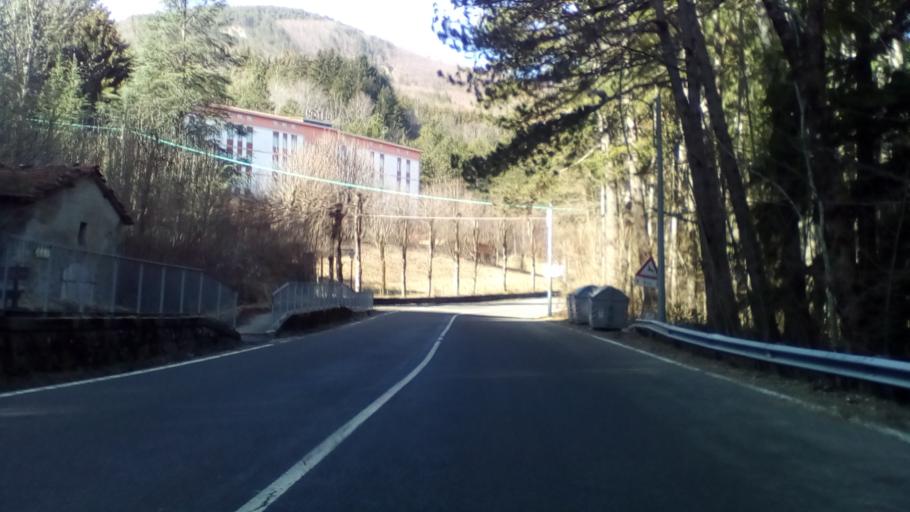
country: IT
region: Emilia-Romagna
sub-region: Provincia di Modena
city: Pievepelago
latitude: 44.2085
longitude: 10.6106
